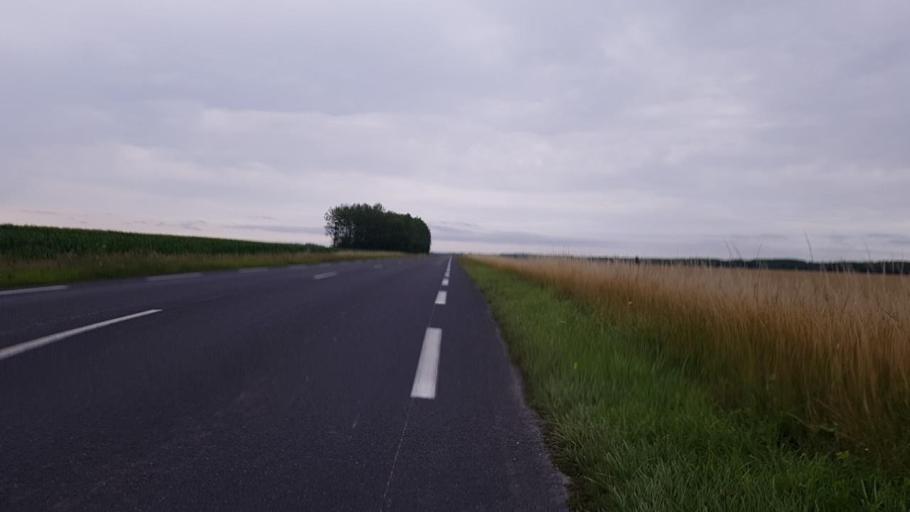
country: FR
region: Champagne-Ardenne
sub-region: Departement de la Marne
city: Pargny-sur-Saulx
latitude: 48.7600
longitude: 4.7719
